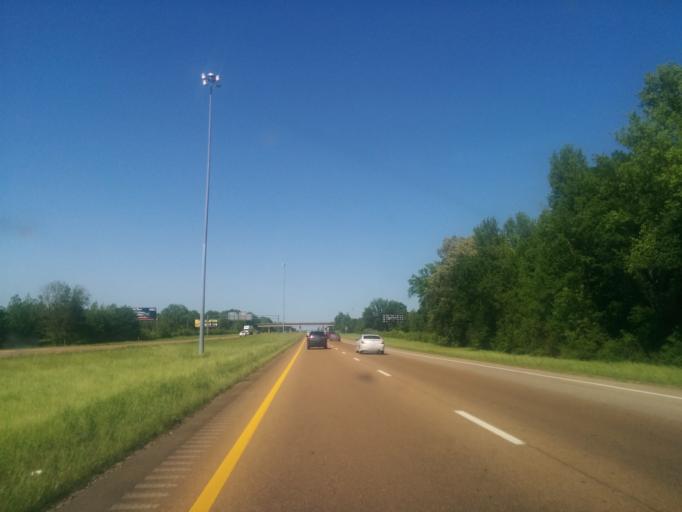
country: US
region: Mississippi
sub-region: Madison County
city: Canton
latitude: 32.5461
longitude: -90.0915
